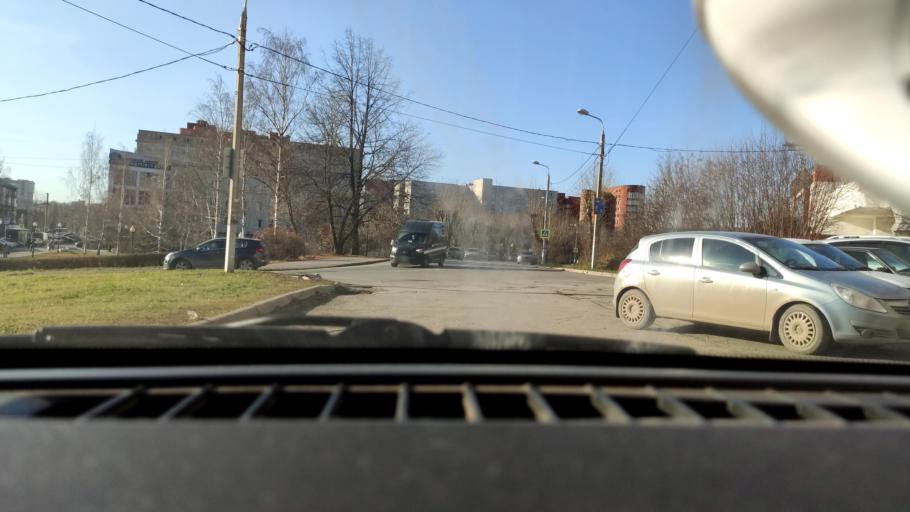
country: RU
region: Perm
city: Perm
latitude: 58.0066
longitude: 56.2006
